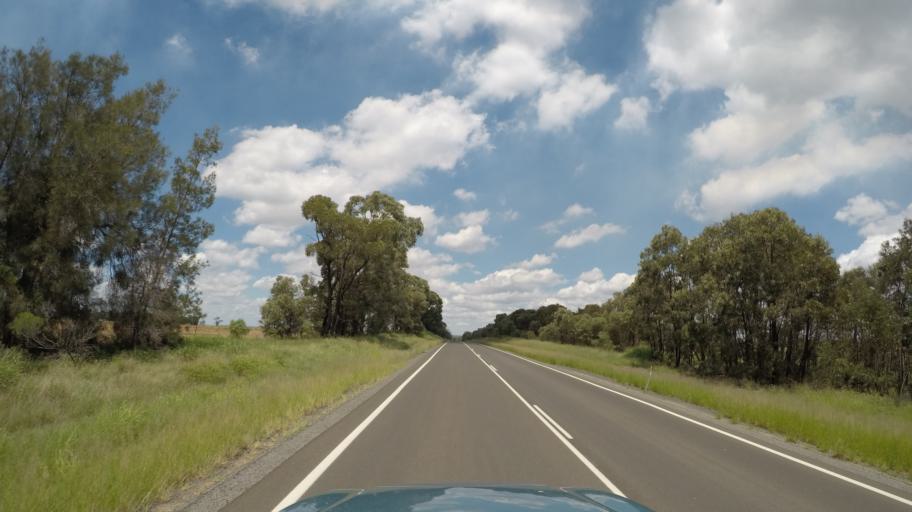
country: AU
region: Queensland
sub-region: Toowoomba
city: Oakey
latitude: -27.9435
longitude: 151.1537
